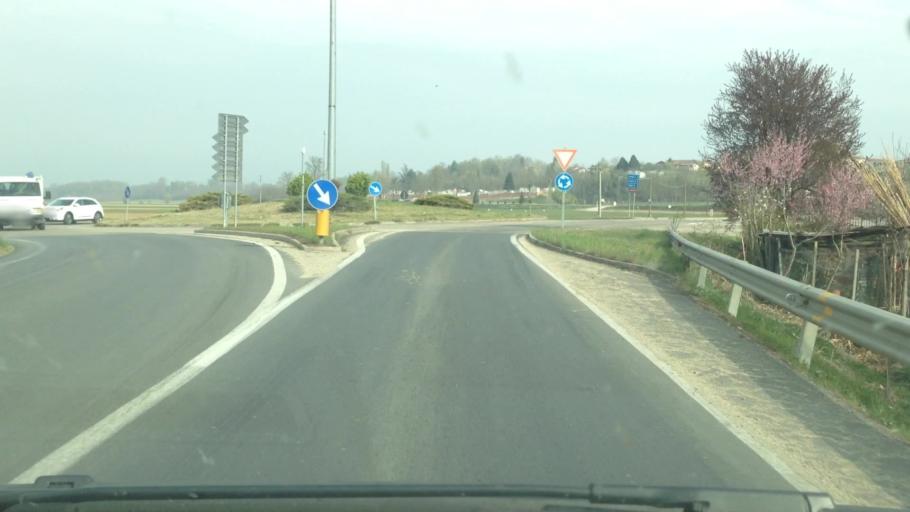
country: IT
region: Piedmont
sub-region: Provincia di Torino
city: Pralormo
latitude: 44.8617
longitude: 7.8962
